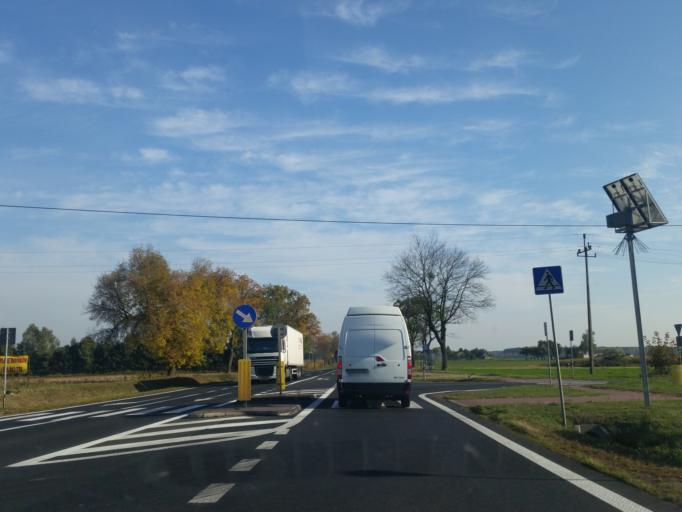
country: PL
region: Masovian Voivodeship
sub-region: Powiat sierpecki
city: Zawidz
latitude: 52.7983
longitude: 19.8611
